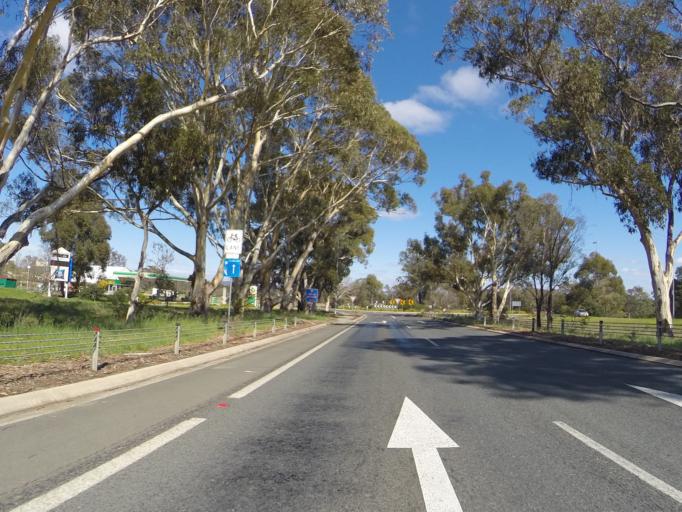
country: AU
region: Australian Capital Territory
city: Kaleen
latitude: -35.2243
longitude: 149.1668
